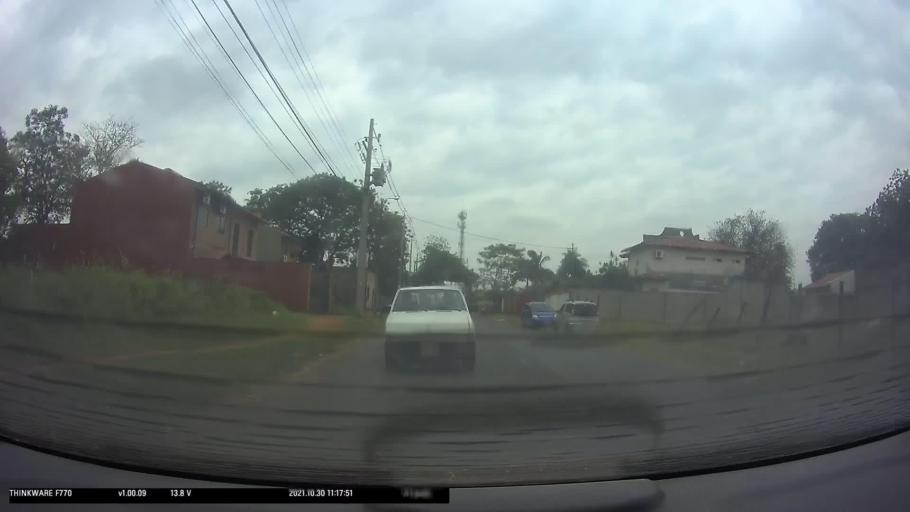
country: PY
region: Central
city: Fernando de la Mora
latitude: -25.3161
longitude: -57.5192
